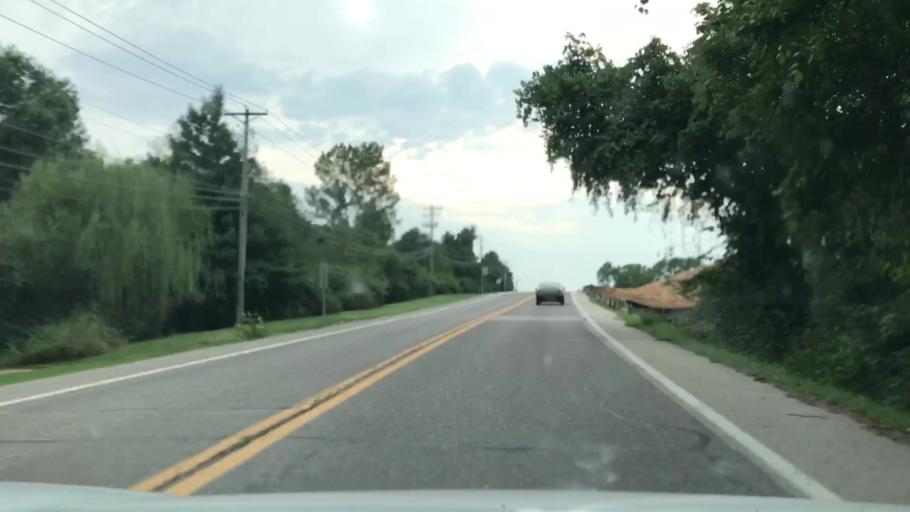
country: US
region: Missouri
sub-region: Saint Louis County
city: Chesterfield
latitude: 38.6542
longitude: -90.6001
